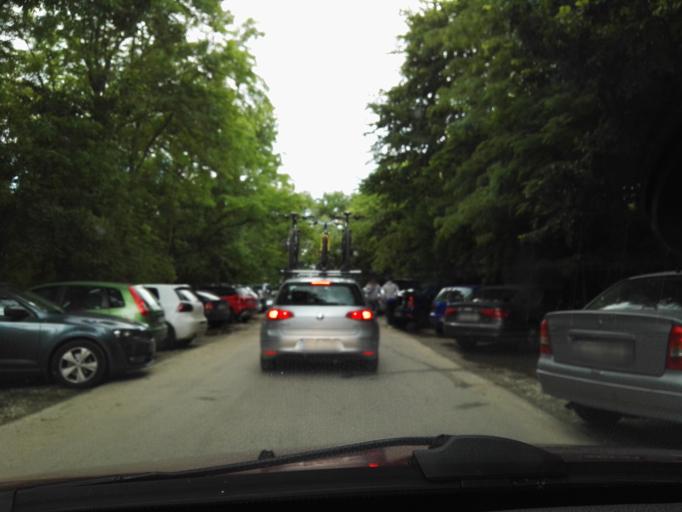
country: RO
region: Giurgiu
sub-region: Comuna Comana
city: Comana
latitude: 44.1718
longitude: 26.1326
